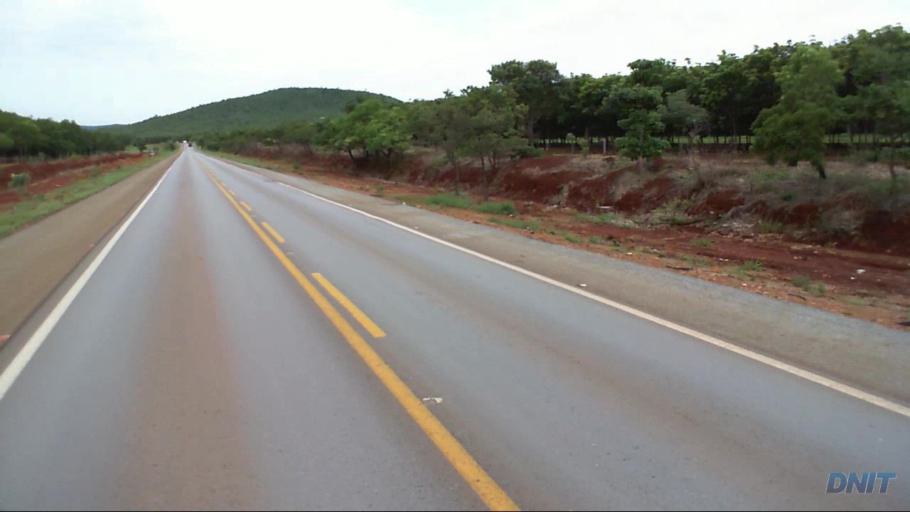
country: BR
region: Goias
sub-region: Barro Alto
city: Barro Alto
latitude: -14.9041
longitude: -48.9621
